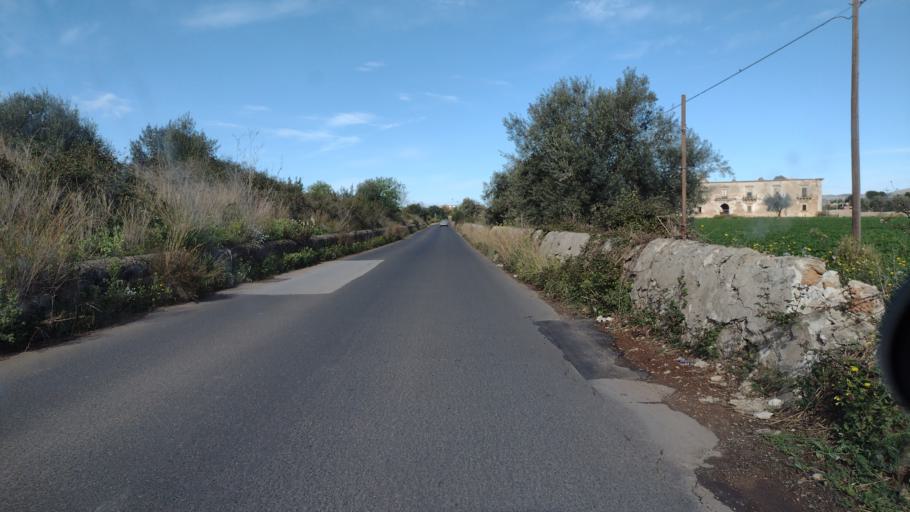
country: IT
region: Sicily
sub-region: Provincia di Siracusa
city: Avola
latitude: 36.8731
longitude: 15.1189
